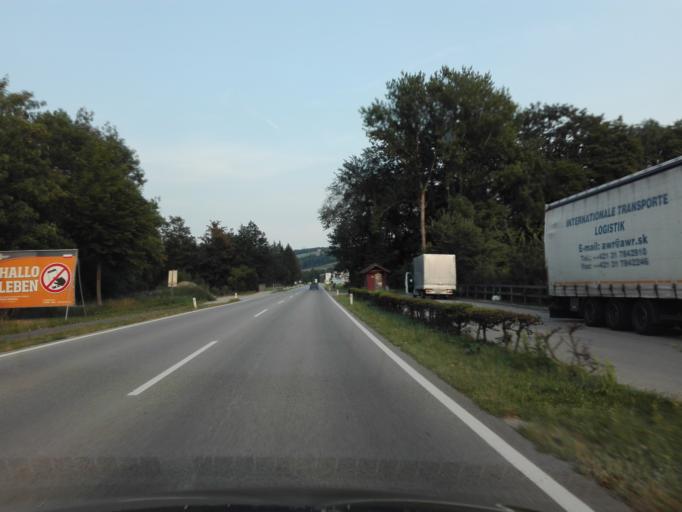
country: AT
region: Upper Austria
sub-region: Politischer Bezirk Grieskirchen
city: Grieskirchen
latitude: 48.2202
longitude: 13.8748
